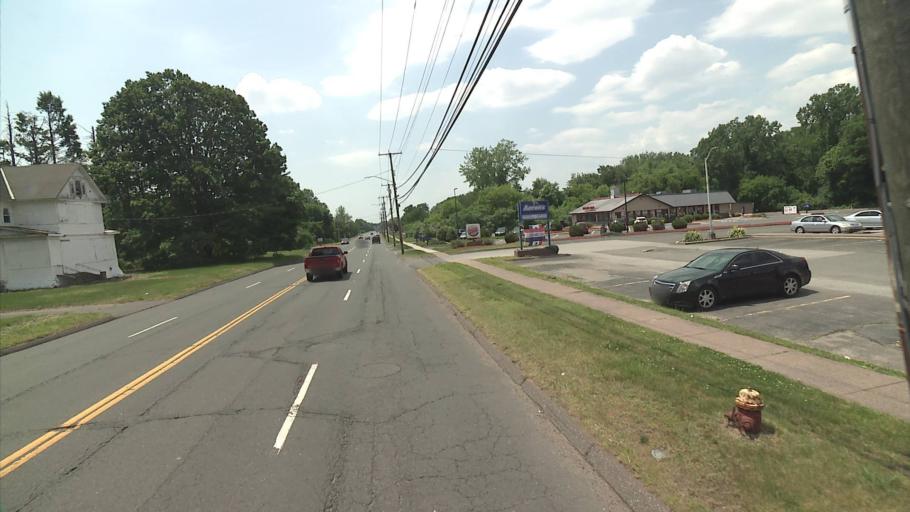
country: US
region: Connecticut
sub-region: Hartford County
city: East Hartford
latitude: 41.7641
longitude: -72.6126
